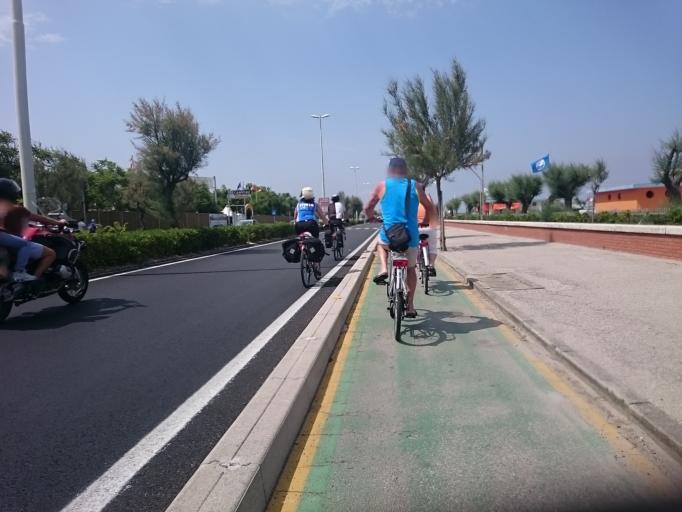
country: IT
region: Veneto
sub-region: Provincia di Venezia
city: Chioggia
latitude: 45.2043
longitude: 12.2995
